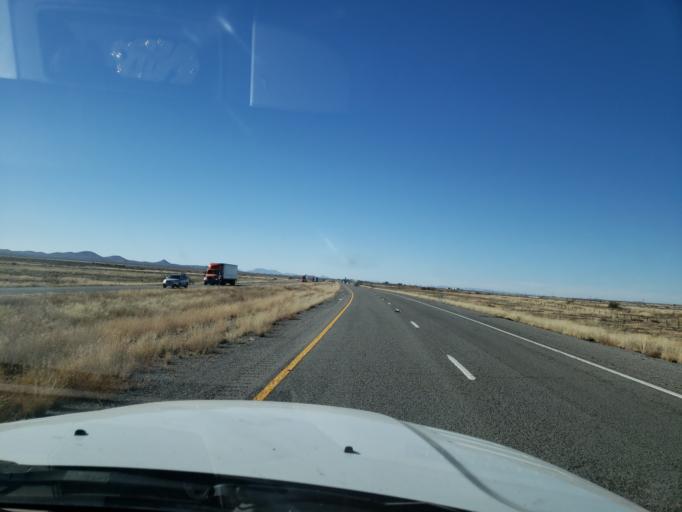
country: US
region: New Mexico
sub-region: Hidalgo County
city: Lordsburg
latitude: 32.3294
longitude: -108.6371
